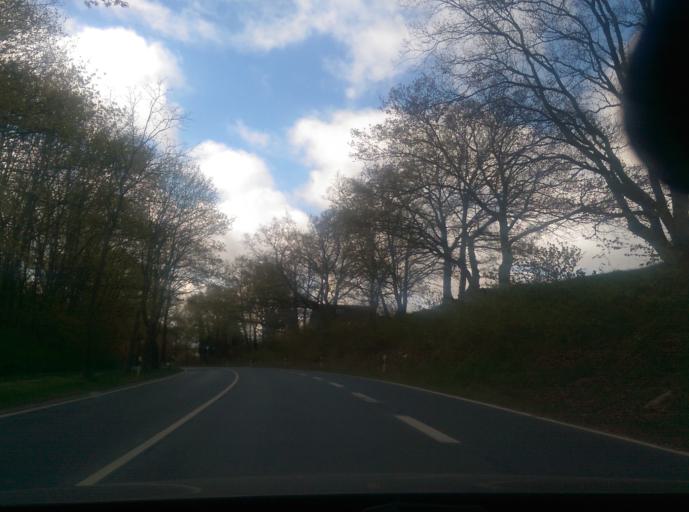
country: DE
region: Lower Saxony
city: Elze
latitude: 52.5528
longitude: 9.7235
